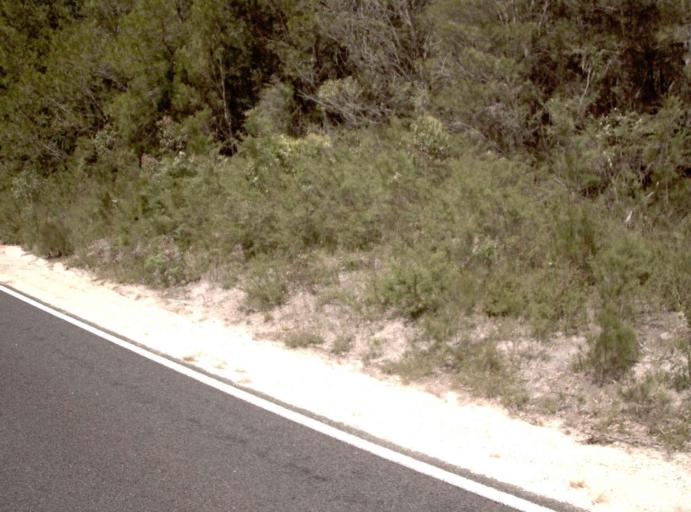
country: AU
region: New South Wales
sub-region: Bega Valley
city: Eden
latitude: -37.4114
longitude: 149.6557
